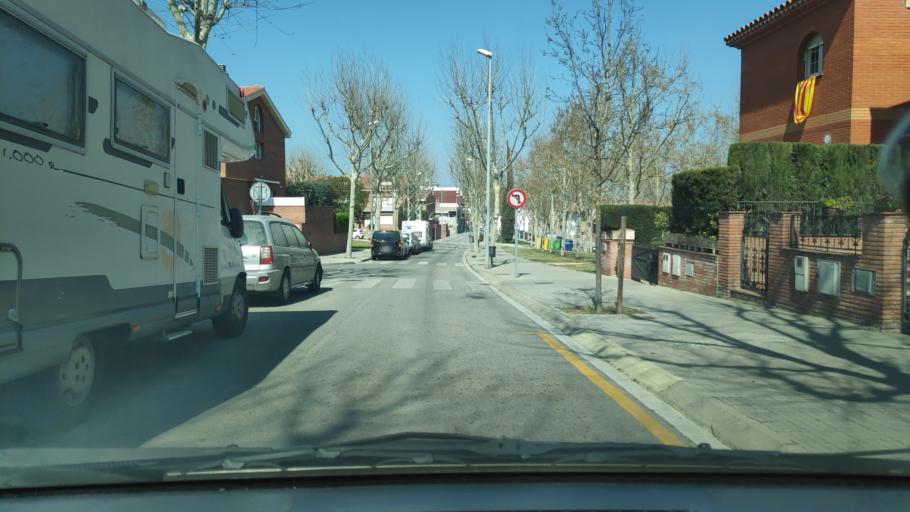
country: ES
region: Catalonia
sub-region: Provincia de Barcelona
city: Mollet del Valles
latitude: 41.5391
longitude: 2.2047
